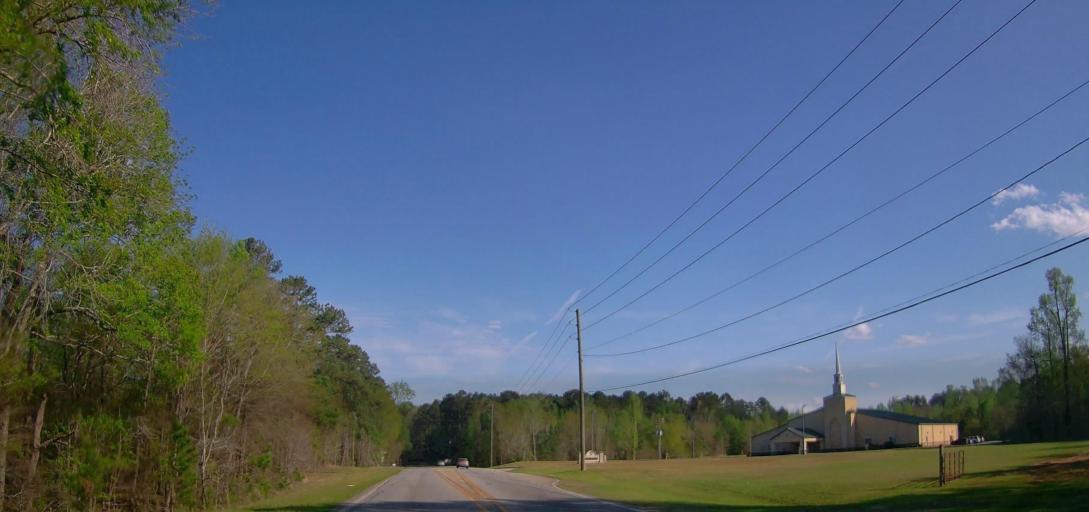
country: US
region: Georgia
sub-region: Baldwin County
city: Milledgeville
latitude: 33.1359
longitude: -83.2358
